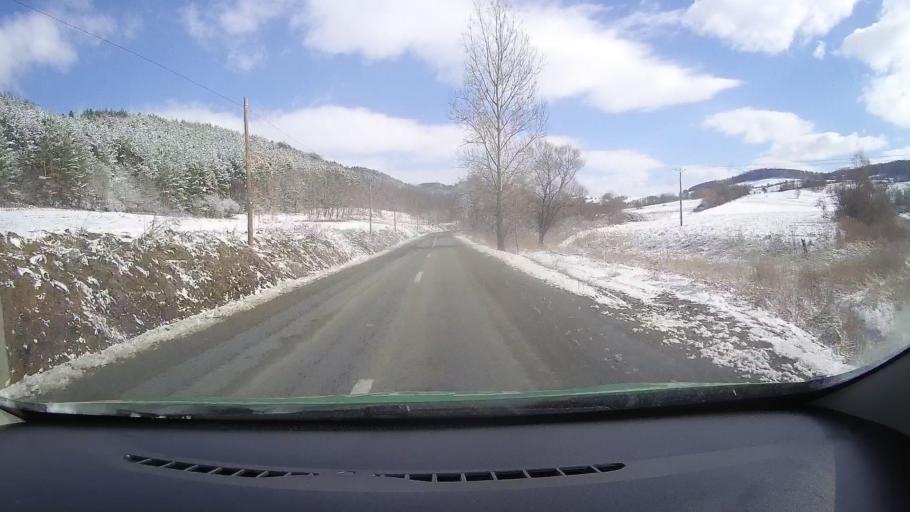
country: RO
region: Sibiu
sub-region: Comuna Barghis
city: Barghis
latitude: 45.9854
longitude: 24.4980
